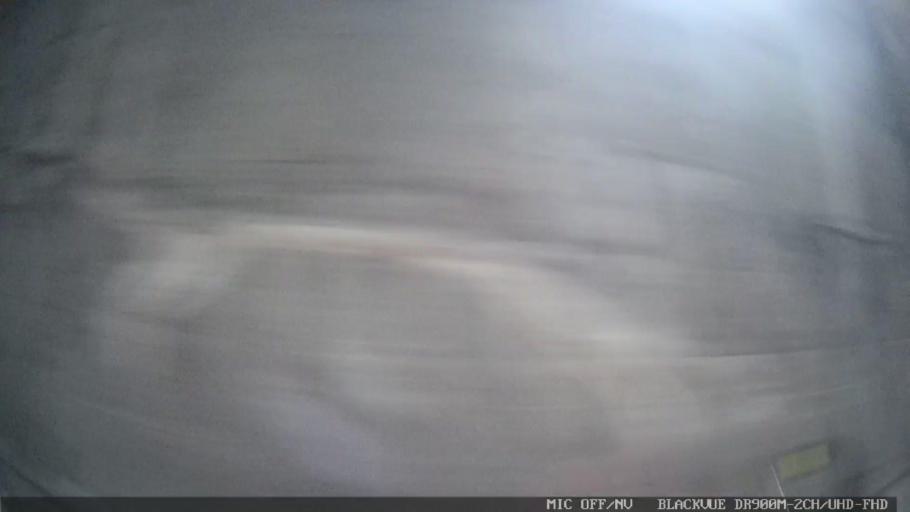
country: BR
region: Sao Paulo
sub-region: Cubatao
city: Cubatao
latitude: -23.8932
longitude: -46.5065
